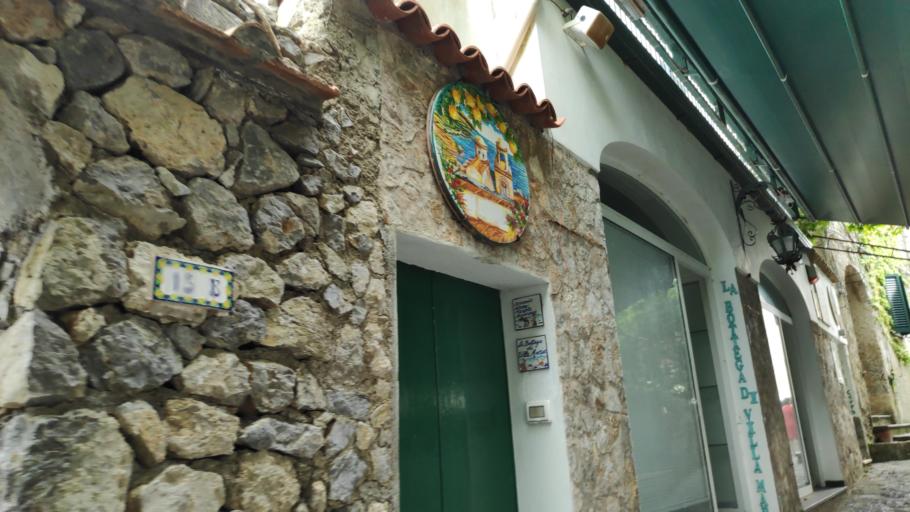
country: IT
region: Campania
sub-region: Provincia di Salerno
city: Ravello
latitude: 40.6470
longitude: 14.6110
